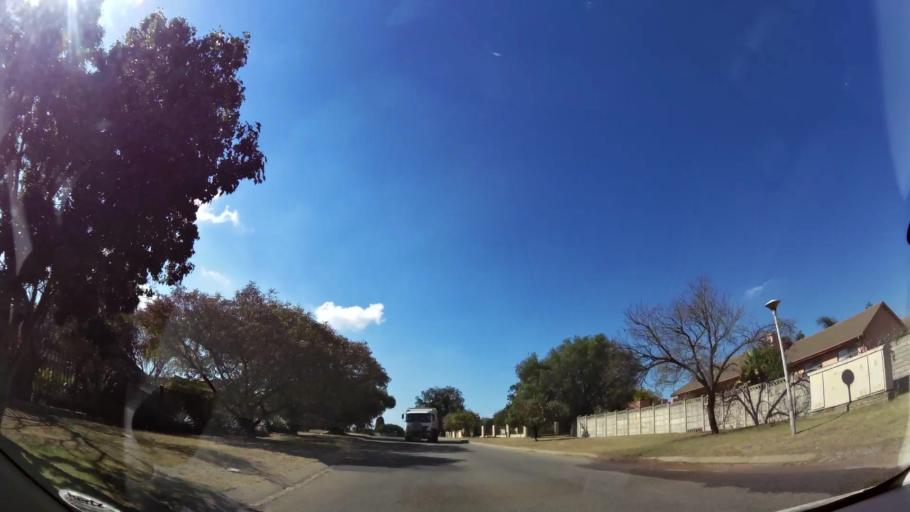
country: ZA
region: Mpumalanga
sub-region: Nkangala District Municipality
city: Witbank
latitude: -25.8590
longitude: 29.2388
